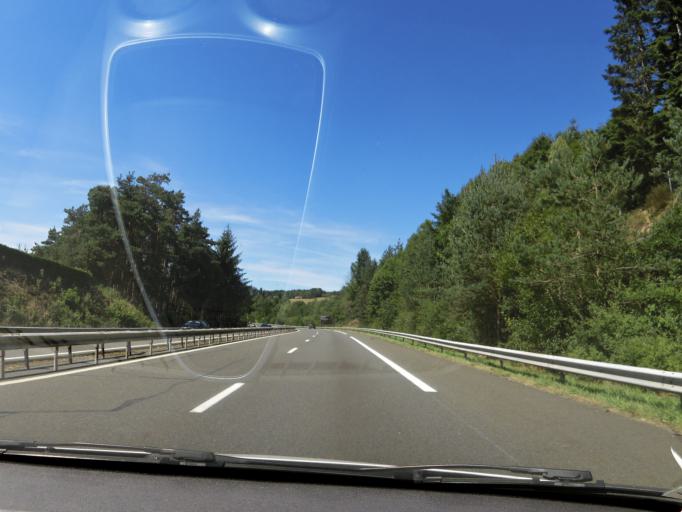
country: FR
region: Auvergne
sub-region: Departement du Puy-de-Dome
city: Celles-sur-Durolle
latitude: 45.8732
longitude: 3.6604
